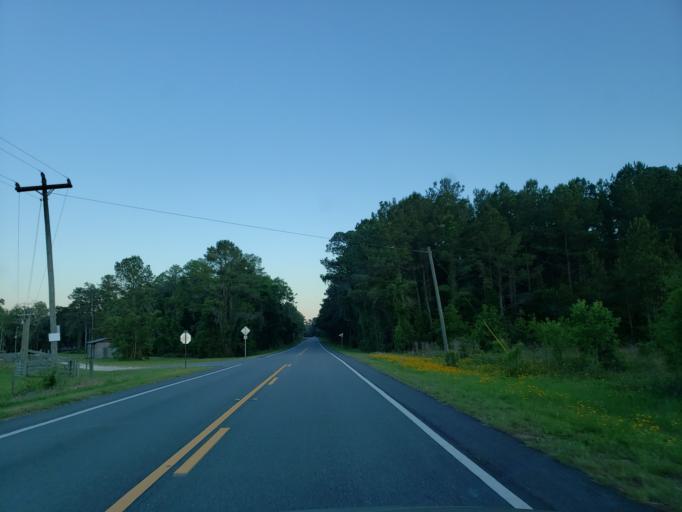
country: US
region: Georgia
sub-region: Echols County
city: Statenville
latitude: 30.5796
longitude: -83.1688
